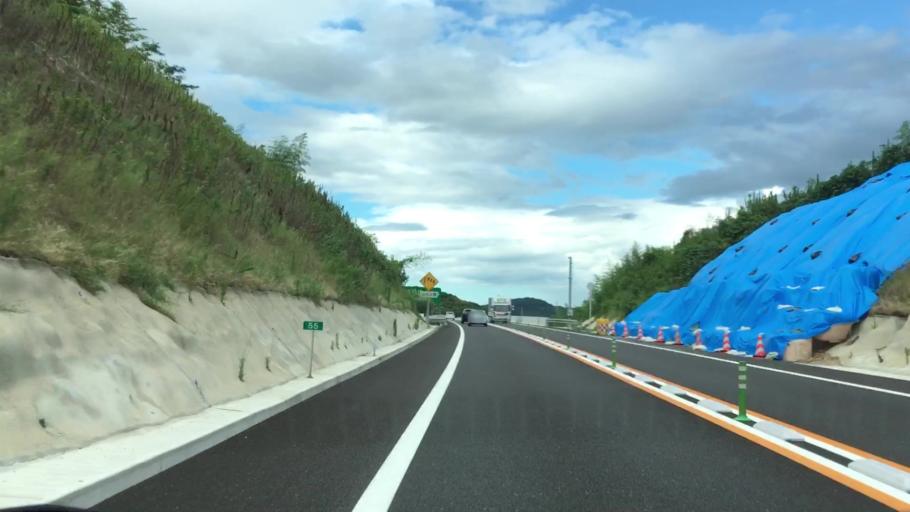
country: JP
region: Saga Prefecture
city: Imaricho-ko
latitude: 33.3225
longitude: 129.9264
